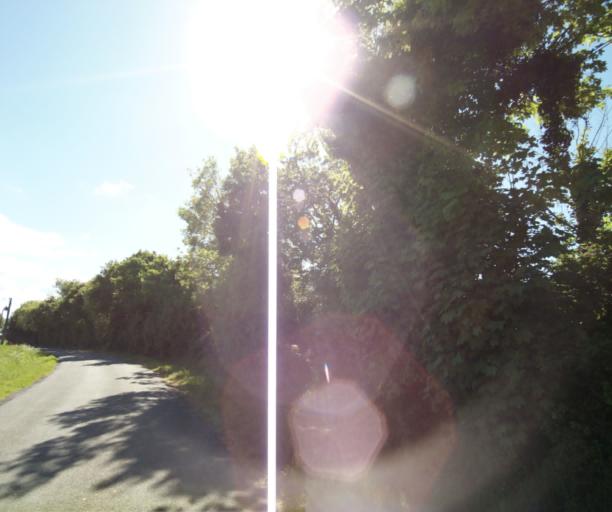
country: FR
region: Poitou-Charentes
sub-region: Departement de la Charente-Maritime
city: Saint-Georges-des-Coteaux
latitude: 45.7952
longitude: -0.6886
